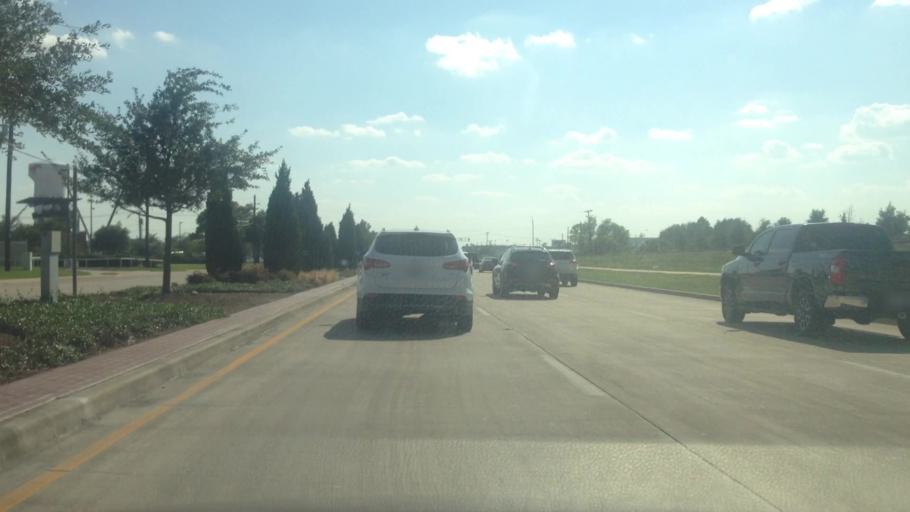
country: US
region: Texas
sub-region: Tarrant County
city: Southlake
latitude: 32.9239
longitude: -97.1112
